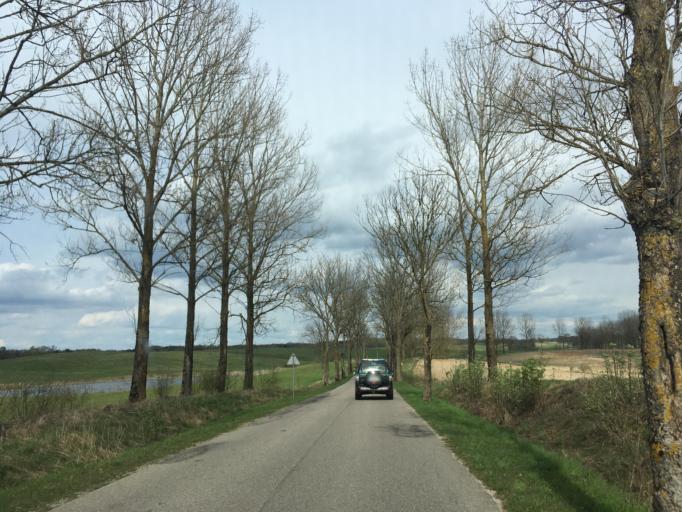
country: PL
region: Podlasie
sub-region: Powiat suwalski
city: Filipow
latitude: 54.3562
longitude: 22.7630
